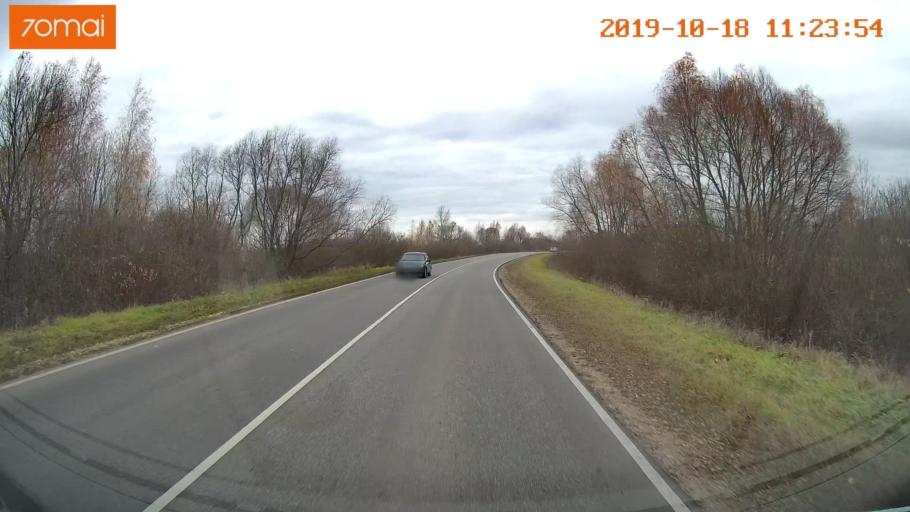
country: RU
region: Tula
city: Kimovsk
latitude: 54.1083
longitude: 38.5946
